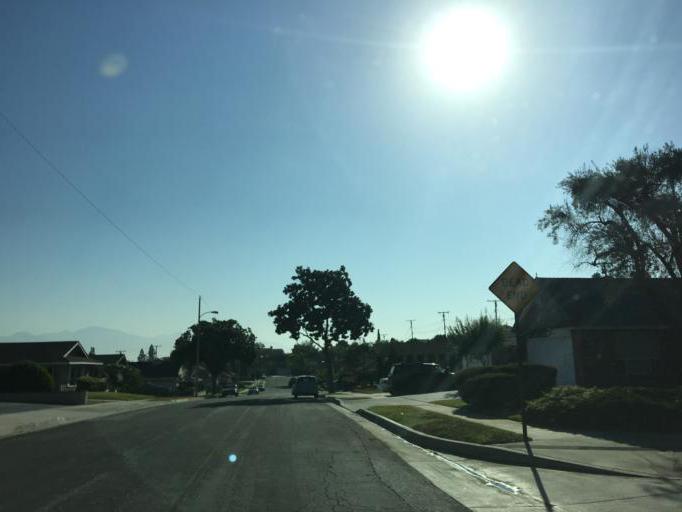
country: US
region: California
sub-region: Los Angeles County
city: Avocado Heights
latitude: 34.0395
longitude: -118.0062
